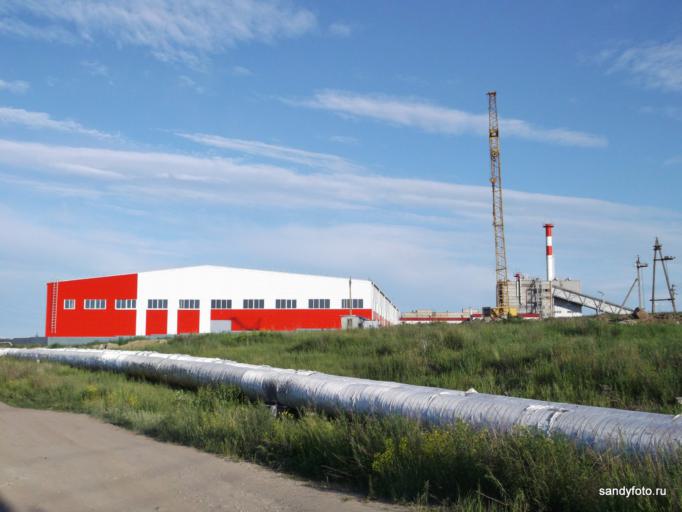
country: RU
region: Chelyabinsk
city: Troitsk
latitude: 54.0681
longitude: 61.5818
